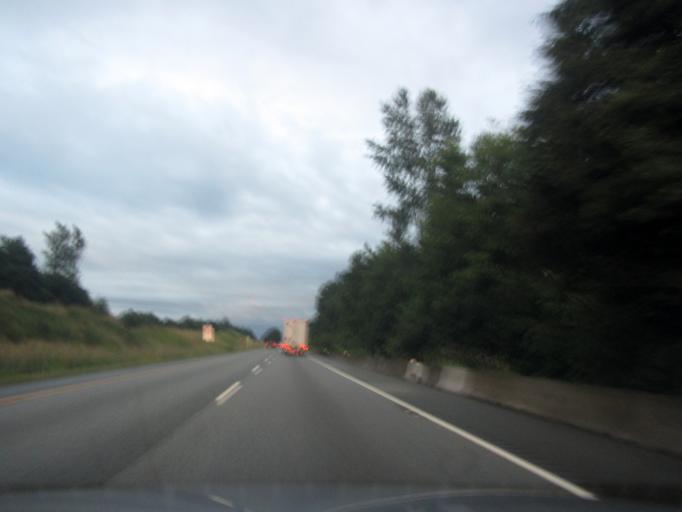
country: CA
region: British Columbia
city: Aldergrove
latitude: 49.0712
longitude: -122.4162
